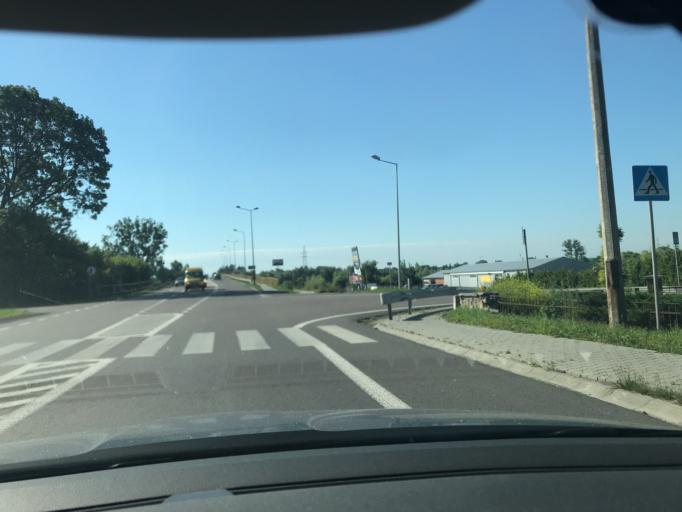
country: PL
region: Lublin Voivodeship
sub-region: Zamosc
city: Zamosc
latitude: 50.7514
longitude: 23.2405
